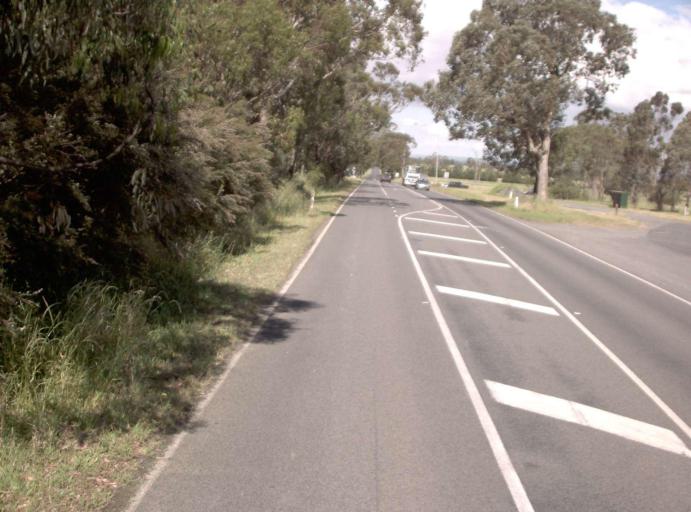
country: AU
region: Victoria
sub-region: Latrobe
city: Traralgon
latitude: -38.1503
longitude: 146.4918
